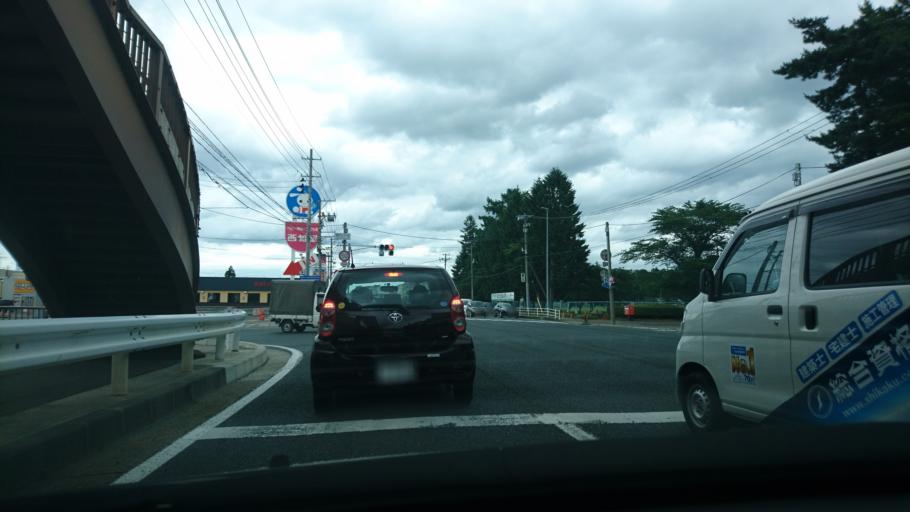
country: JP
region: Iwate
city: Morioka-shi
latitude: 39.7467
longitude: 141.1316
